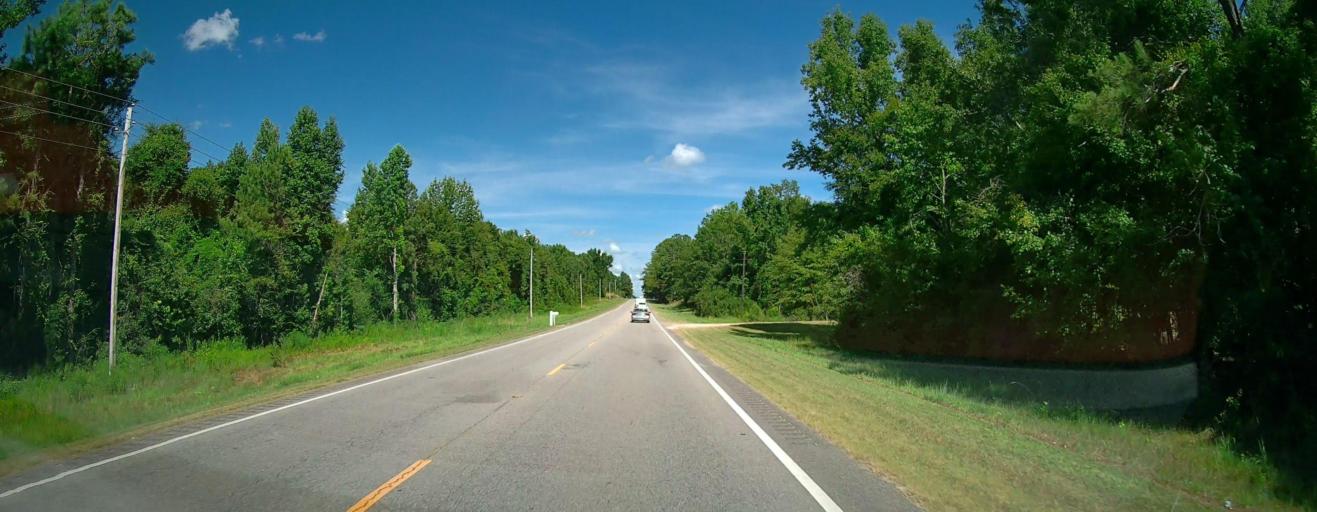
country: US
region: Alabama
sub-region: Elmore County
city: Tallassee
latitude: 32.3995
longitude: -85.9379
